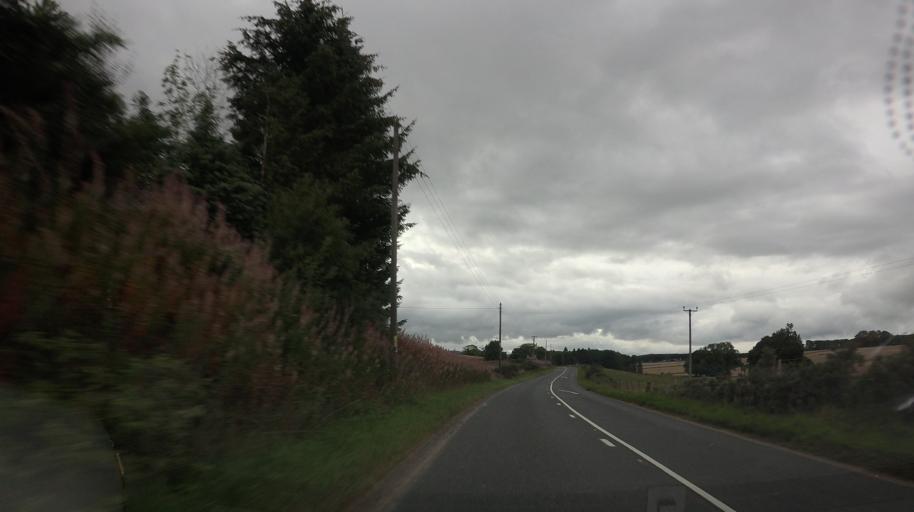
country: GB
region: Scotland
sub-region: Aberdeenshire
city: Kemnay
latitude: 57.1811
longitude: -2.4685
